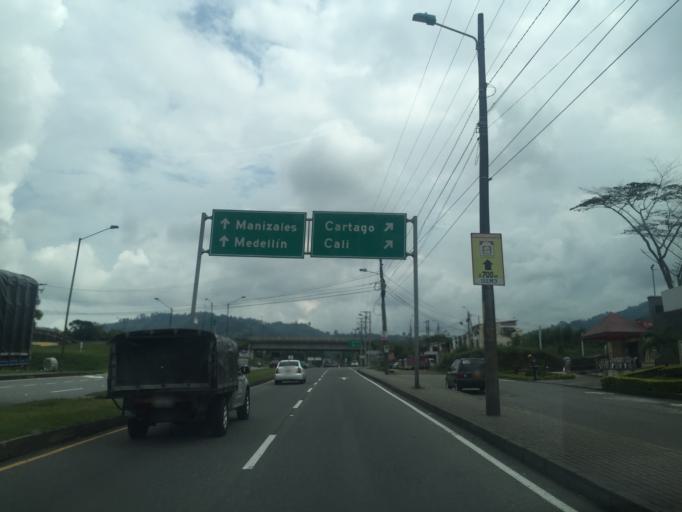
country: CO
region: Risaralda
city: Dos Quebradas
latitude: 4.8485
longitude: -75.6677
